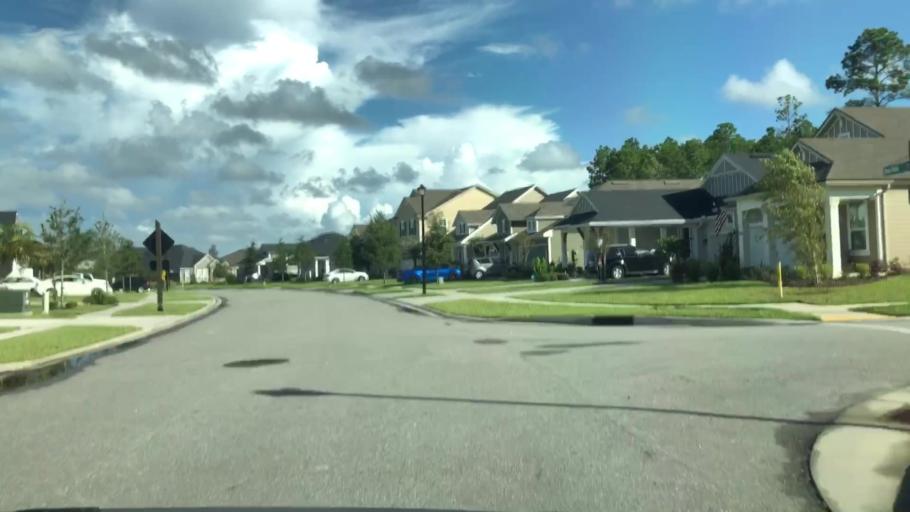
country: US
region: Florida
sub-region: Saint Johns County
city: Palm Valley
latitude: 30.1284
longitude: -81.4081
